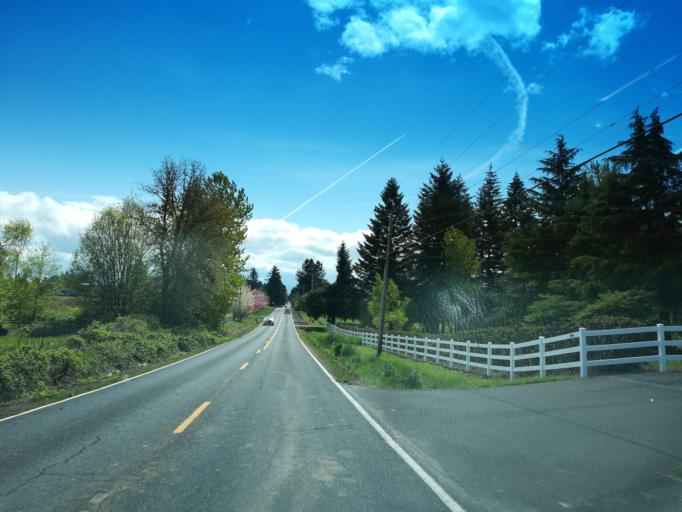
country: US
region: Oregon
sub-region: Clackamas County
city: Damascus
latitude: 45.4434
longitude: -122.4346
